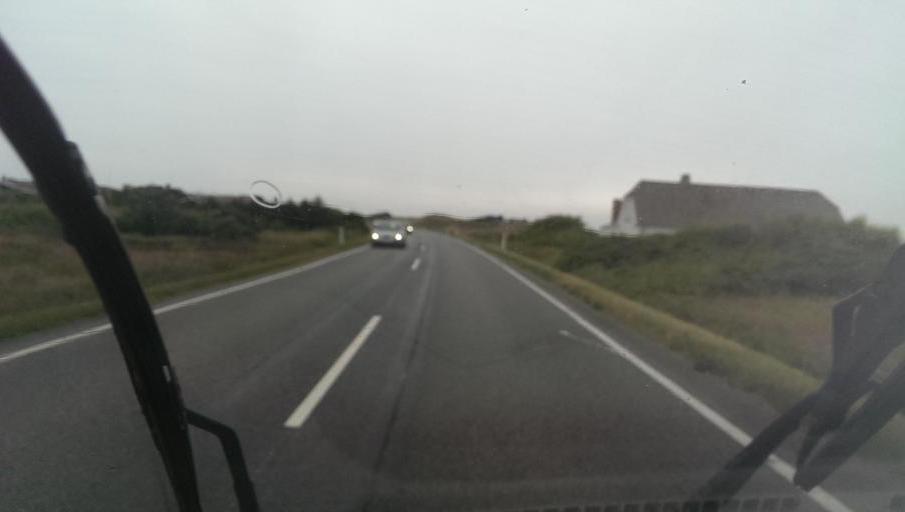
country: DK
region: Central Jutland
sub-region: Ringkobing-Skjern Kommune
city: Hvide Sande
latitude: 55.9277
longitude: 8.1625
